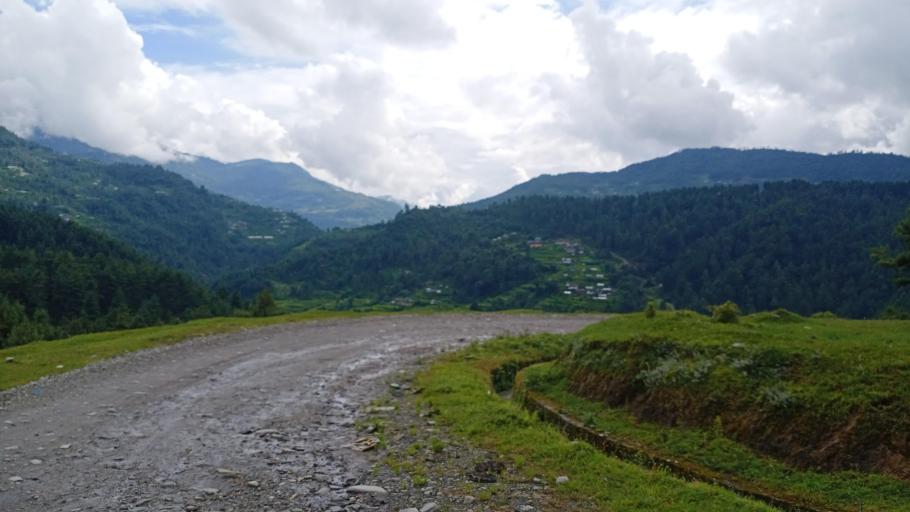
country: NP
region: Central Region
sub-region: Janakpur Zone
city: Ramechhap
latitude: 27.6265
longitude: 86.2350
